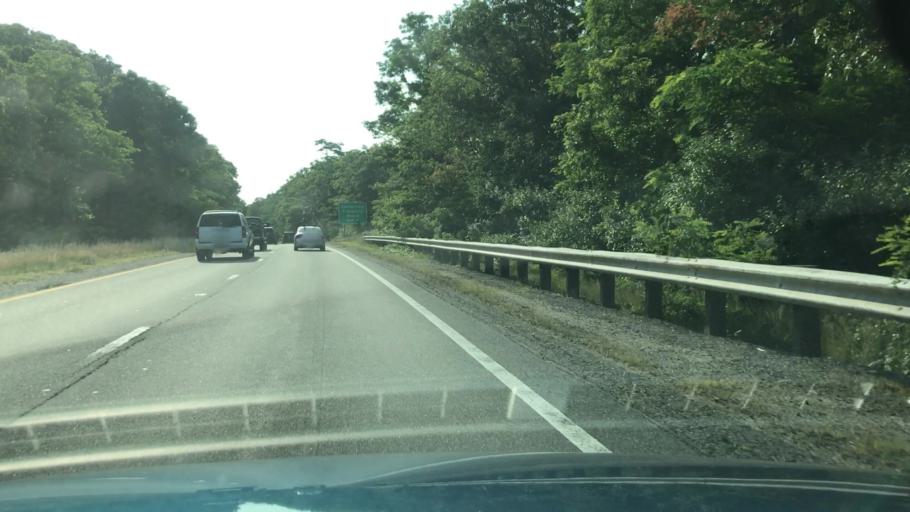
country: US
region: Massachusetts
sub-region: Barnstable County
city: West Barnstable
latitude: 41.6842
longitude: -70.3574
